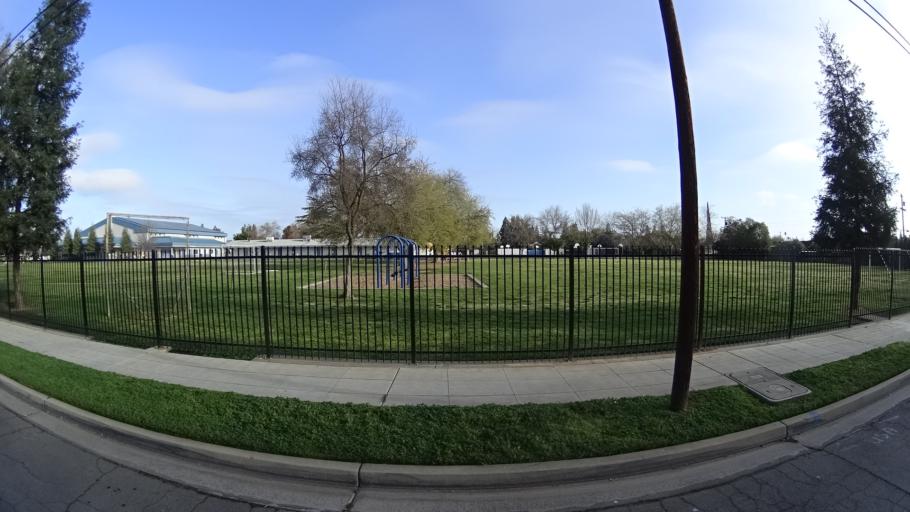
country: US
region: California
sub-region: Fresno County
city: Fresno
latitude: 36.8193
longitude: -119.7979
